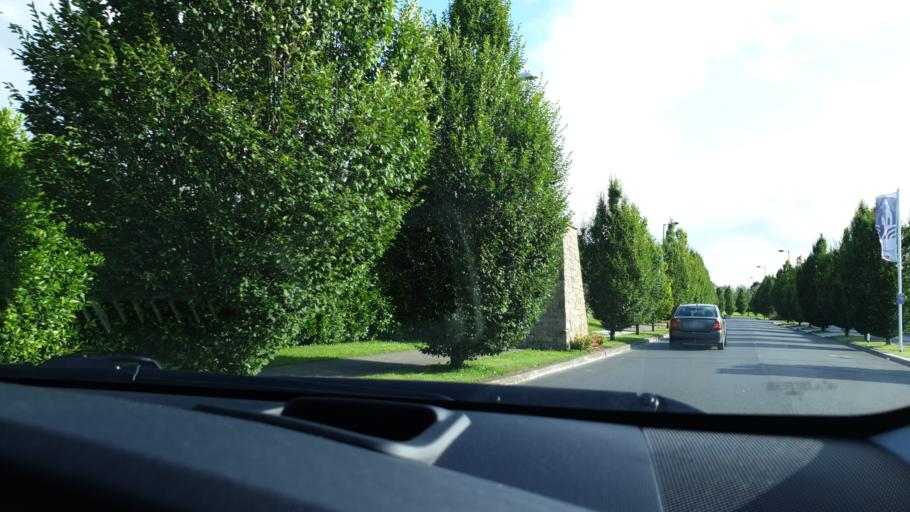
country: IE
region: Leinster
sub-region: An Mhi
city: Ashbourne
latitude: 53.5091
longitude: -6.4040
